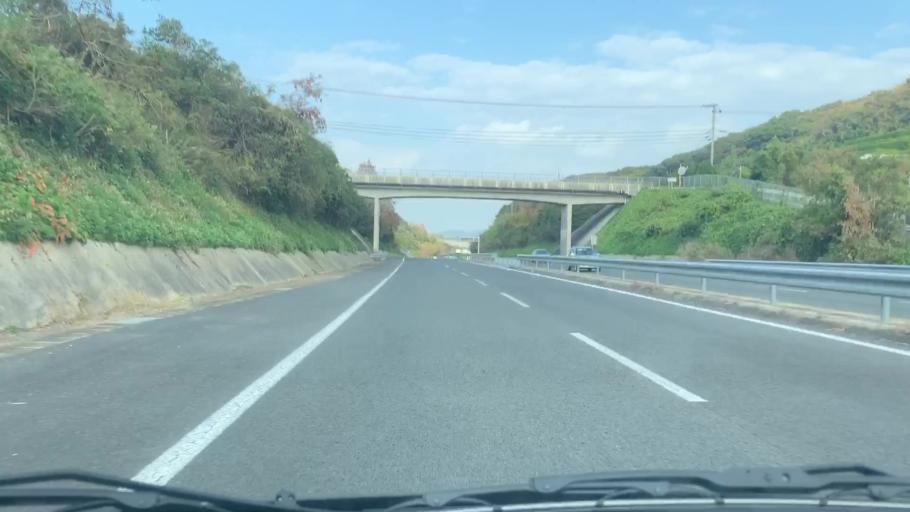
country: JP
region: Nagasaki
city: Sasebo
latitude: 33.0473
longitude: 129.7508
